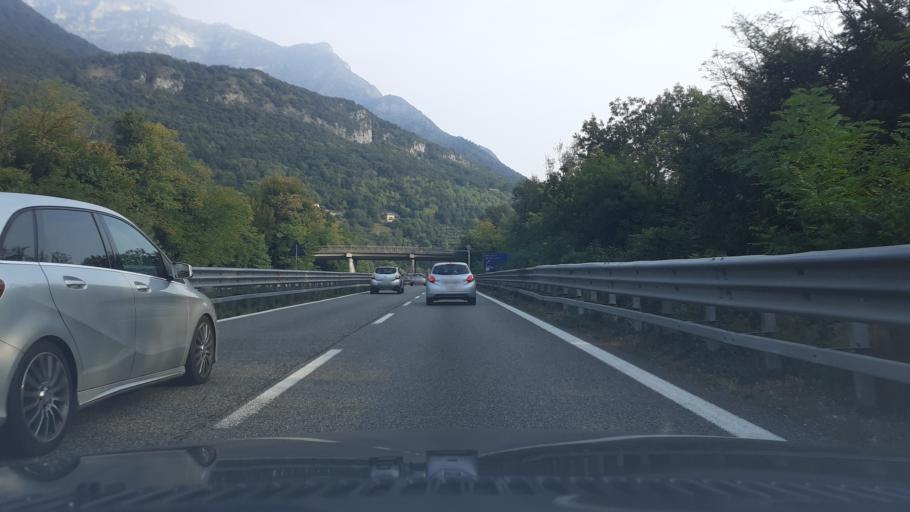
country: IT
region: Lombardy
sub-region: Provincia di Lecco
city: Suello
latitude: 45.8185
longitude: 9.3223
